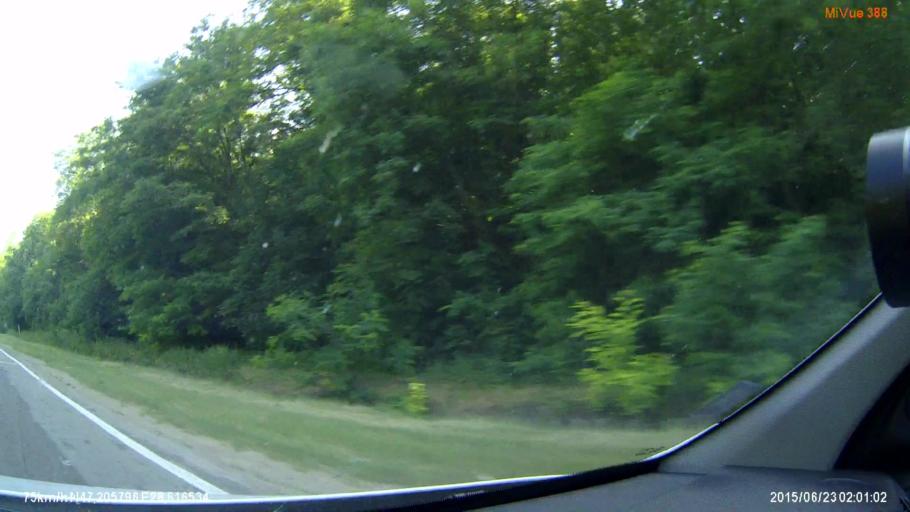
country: MD
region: Straseni
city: Straseni
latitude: 47.2062
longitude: 28.6164
